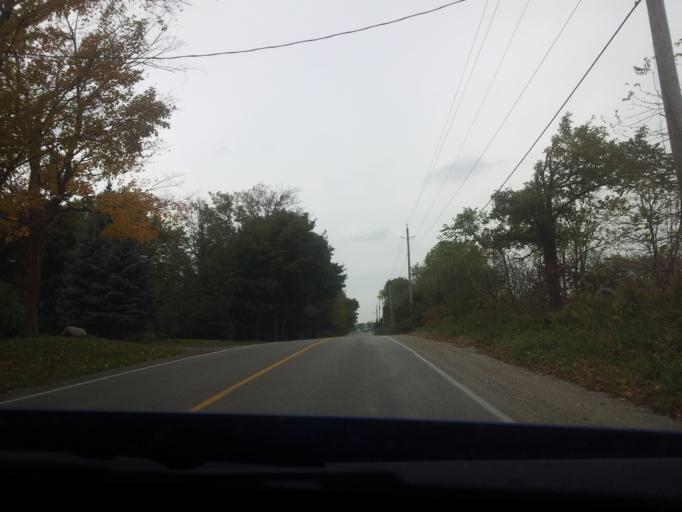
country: CA
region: Ontario
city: London
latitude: 43.0395
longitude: -81.2848
